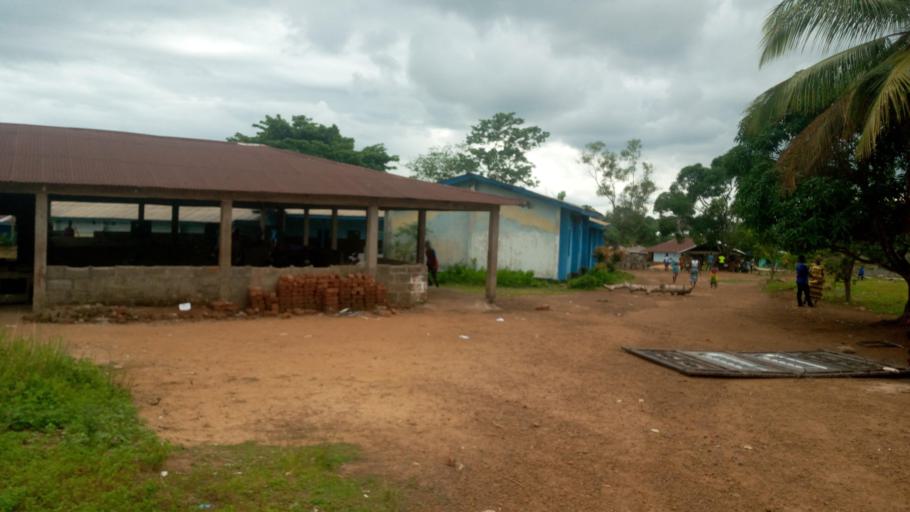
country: SL
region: Southern Province
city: Mogbwemo
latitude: 7.6007
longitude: -12.1776
